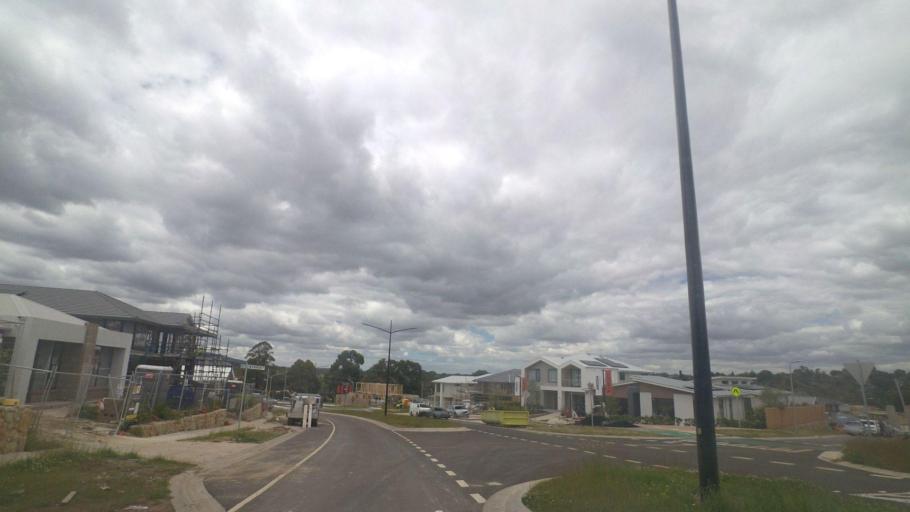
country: AU
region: Victoria
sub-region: Yarra Ranges
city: Lilydale
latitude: -37.7742
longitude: 145.3373
